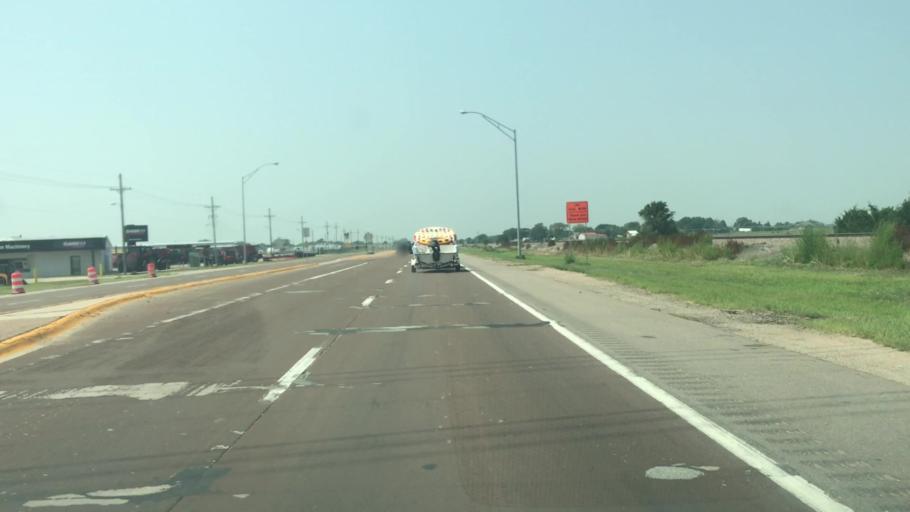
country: US
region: Nebraska
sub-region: Hall County
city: Grand Island
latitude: 40.9545
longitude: -98.3884
